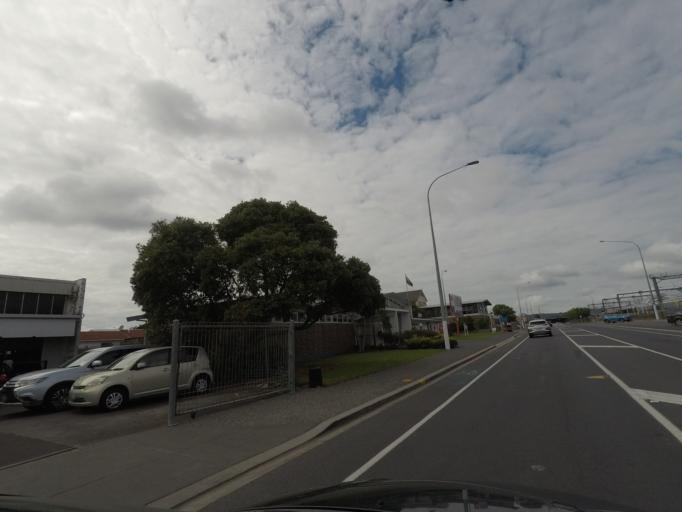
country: NZ
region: Auckland
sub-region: Auckland
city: Rosebank
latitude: -36.8839
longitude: 174.6314
